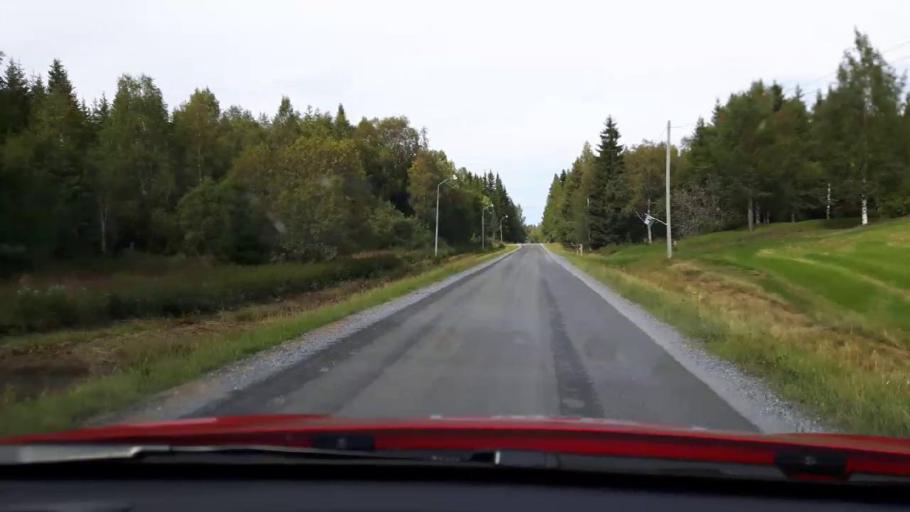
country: SE
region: Jaemtland
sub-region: Krokoms Kommun
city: Valla
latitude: 63.2674
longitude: 13.9051
